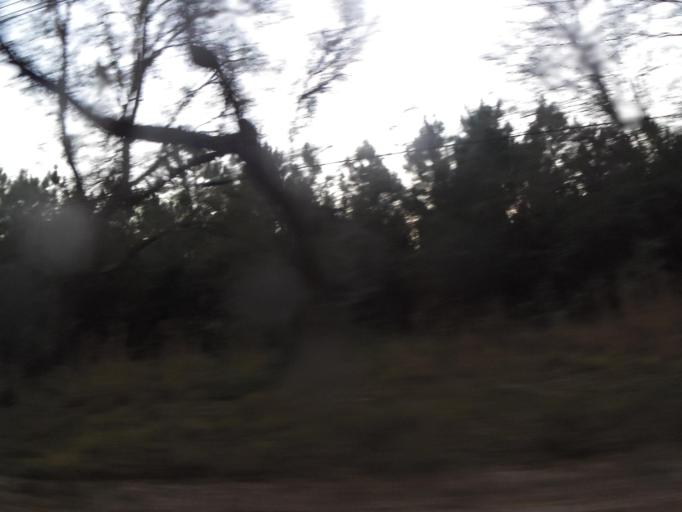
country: US
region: Florida
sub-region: Clay County
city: Asbury Lake
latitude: 29.9817
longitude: -81.7942
